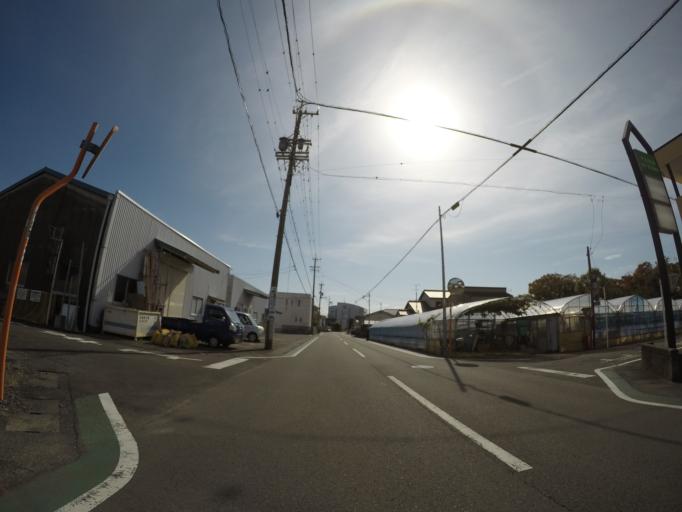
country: JP
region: Shizuoka
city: Shizuoka-shi
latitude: 34.9338
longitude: 138.3776
